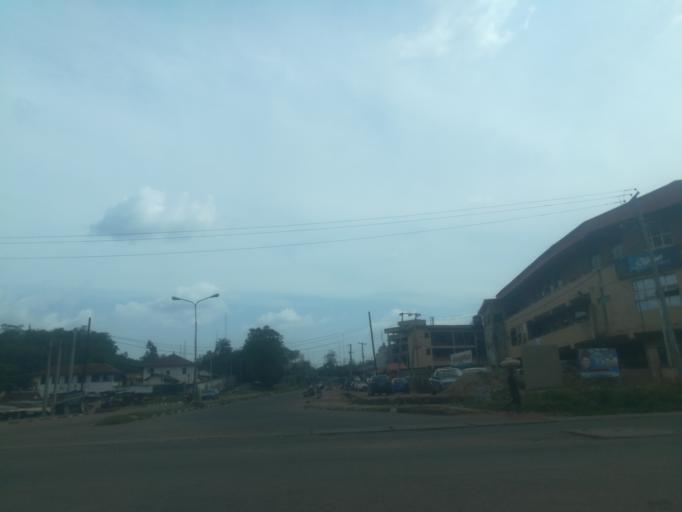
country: NG
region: Ogun
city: Abeokuta
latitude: 7.1419
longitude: 3.3392
